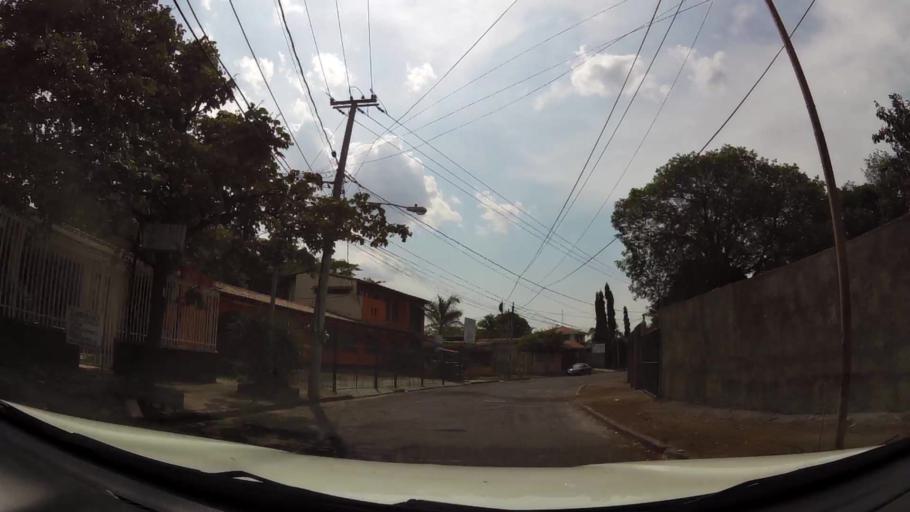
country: NI
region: Managua
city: Managua
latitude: 12.1365
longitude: -86.2801
